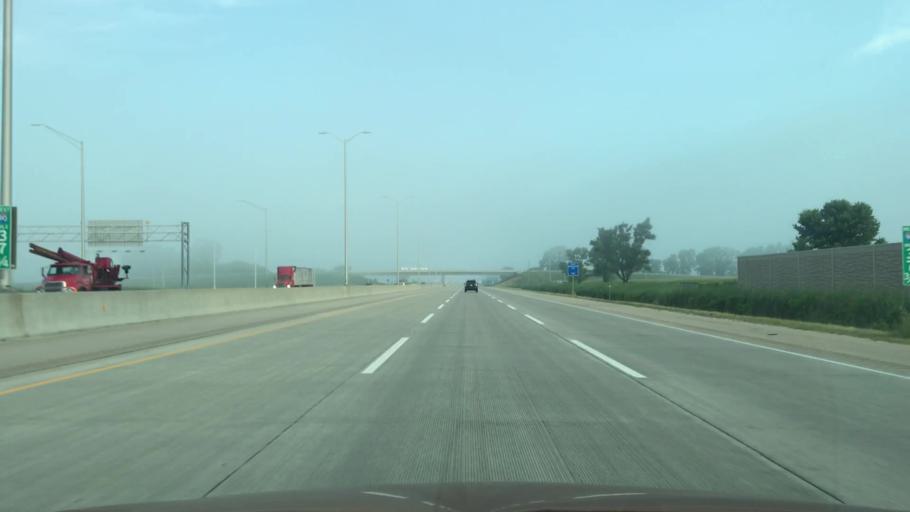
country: US
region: Illinois
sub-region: McHenry County
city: Marengo
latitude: 42.1678
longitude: -88.5893
